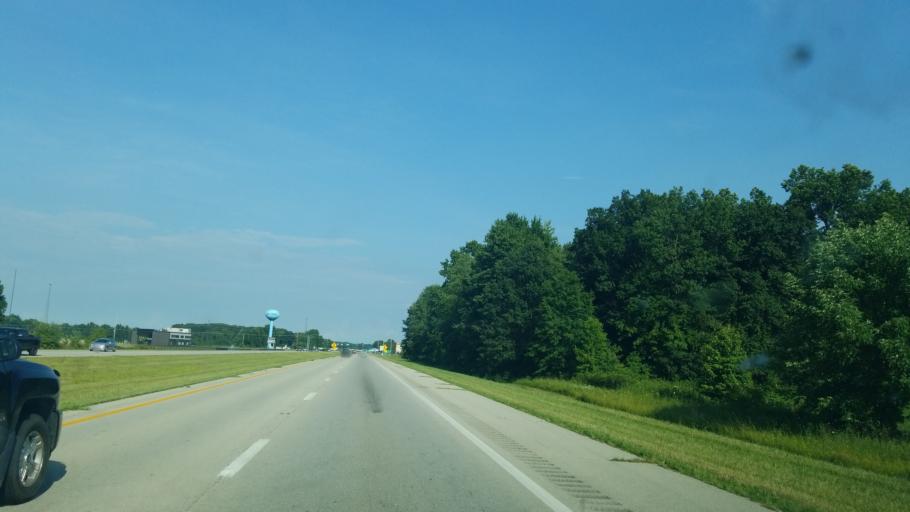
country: US
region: Ohio
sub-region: Brown County
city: Mount Orab
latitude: 39.0477
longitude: -83.9469
